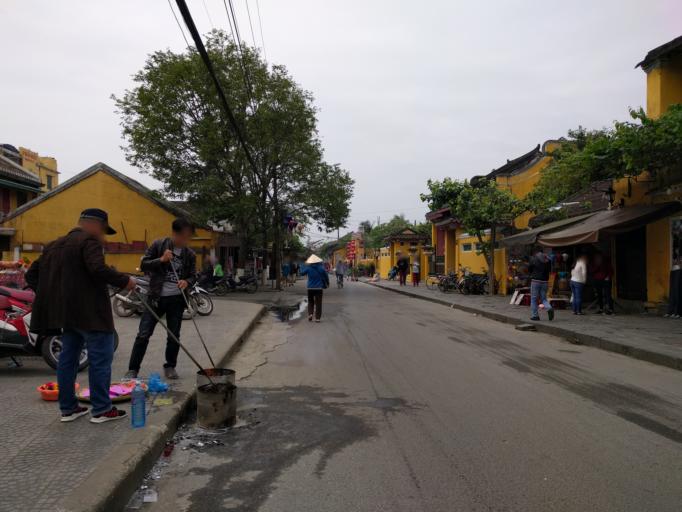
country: VN
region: Quang Nam
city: Hoi An
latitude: 15.8776
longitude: 108.3324
